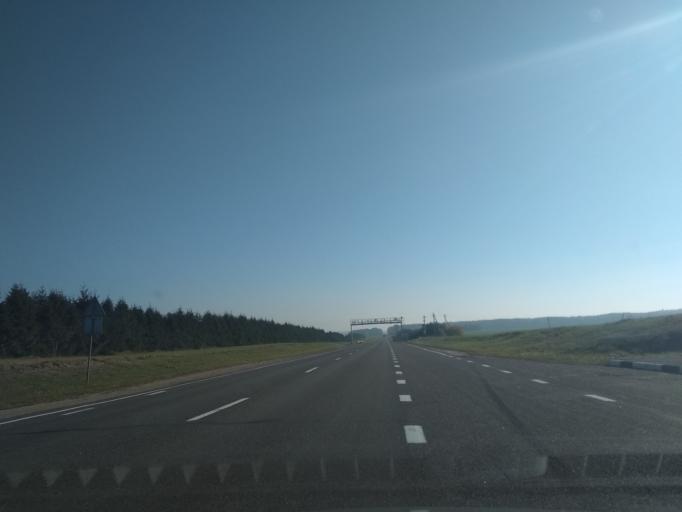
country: BY
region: Grodnenskaya
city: Zel'va
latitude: 53.1350
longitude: 24.9736
